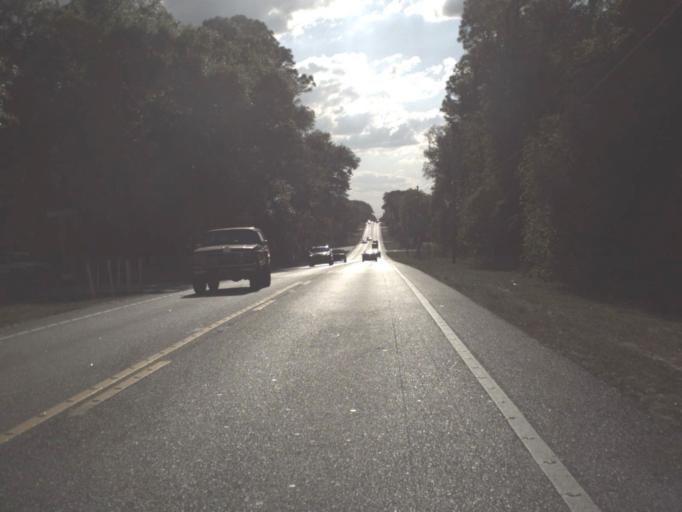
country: US
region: Florida
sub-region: Lake County
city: Mount Plymouth
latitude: 28.8081
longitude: -81.5355
